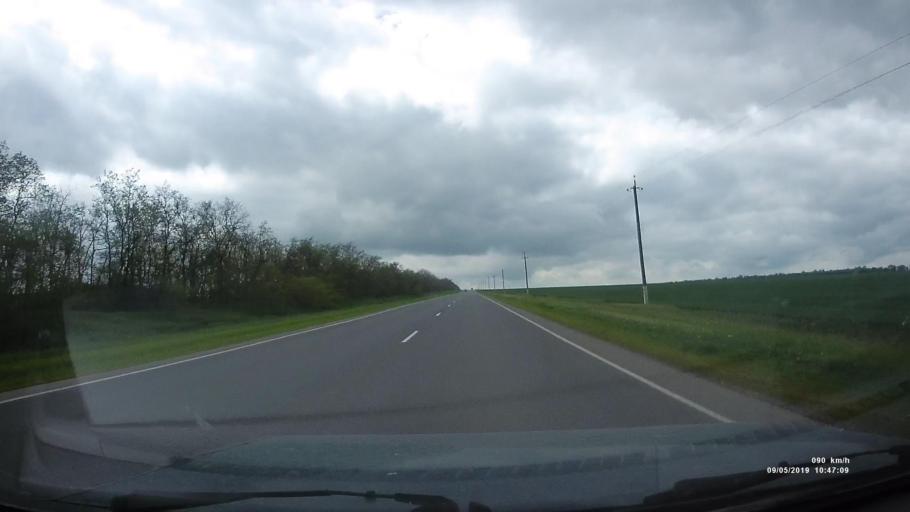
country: RU
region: Rostov
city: Peshkovo
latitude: 46.9747
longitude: 39.3557
